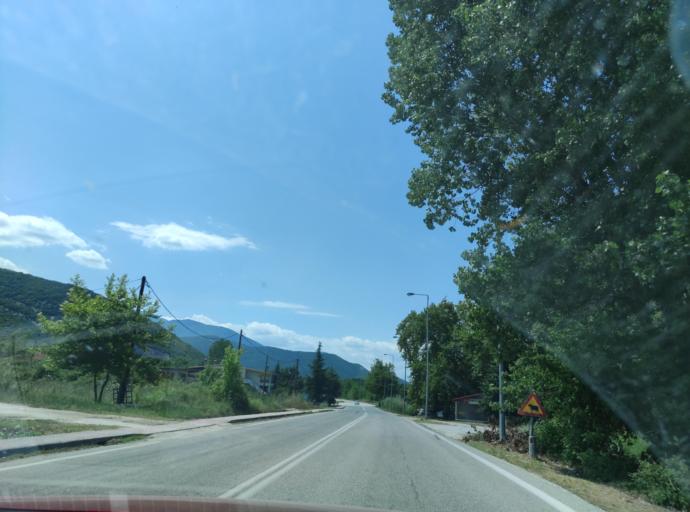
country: GR
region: East Macedonia and Thrace
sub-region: Nomos Kavalas
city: Palaiochori
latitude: 40.9504
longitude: 24.2066
